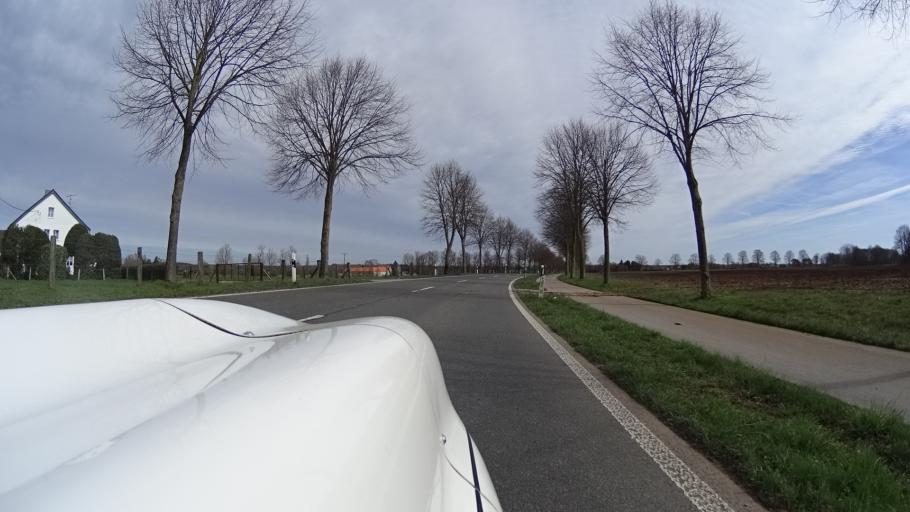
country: NL
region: Limburg
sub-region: Gemeente Gennep
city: Gennep
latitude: 51.7030
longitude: 6.0595
